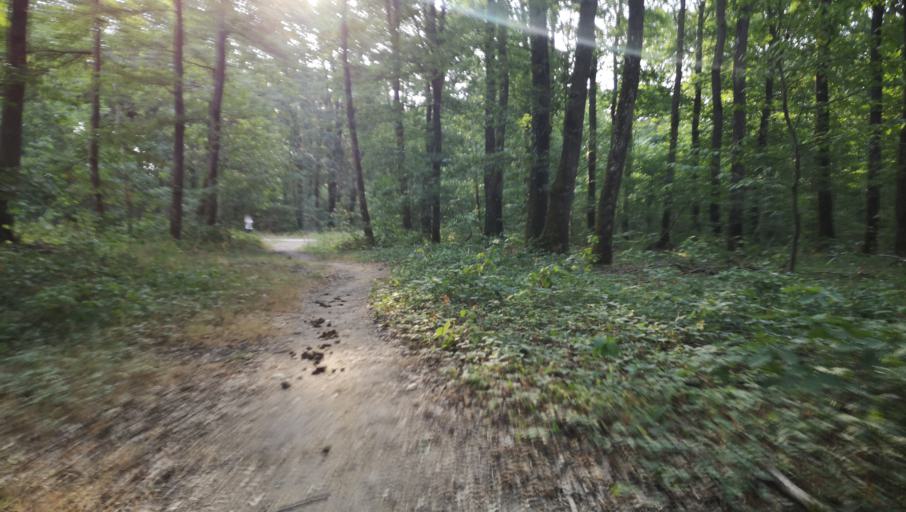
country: FR
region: Centre
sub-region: Departement du Loiret
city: Saint-Jean-de-Braye
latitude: 47.9390
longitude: 1.9786
